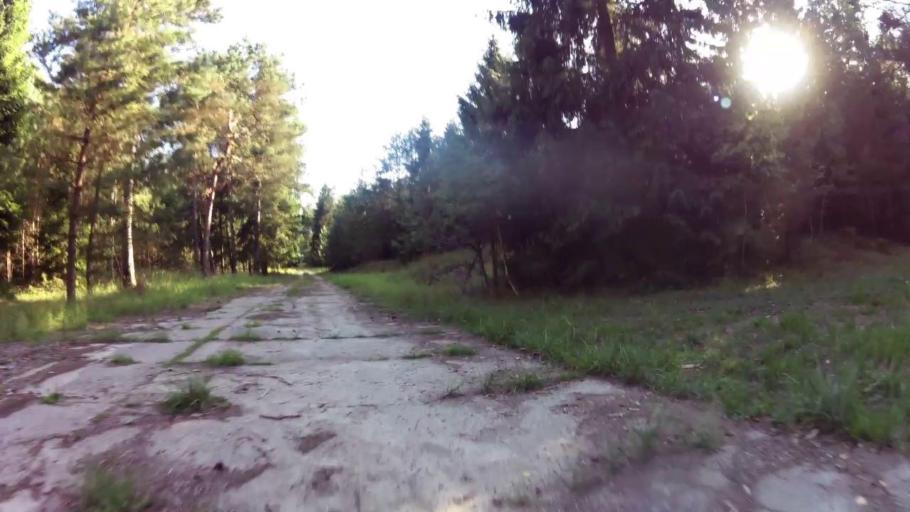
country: PL
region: West Pomeranian Voivodeship
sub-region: Powiat drawski
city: Drawsko Pomorskie
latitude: 53.4641
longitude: 15.8504
